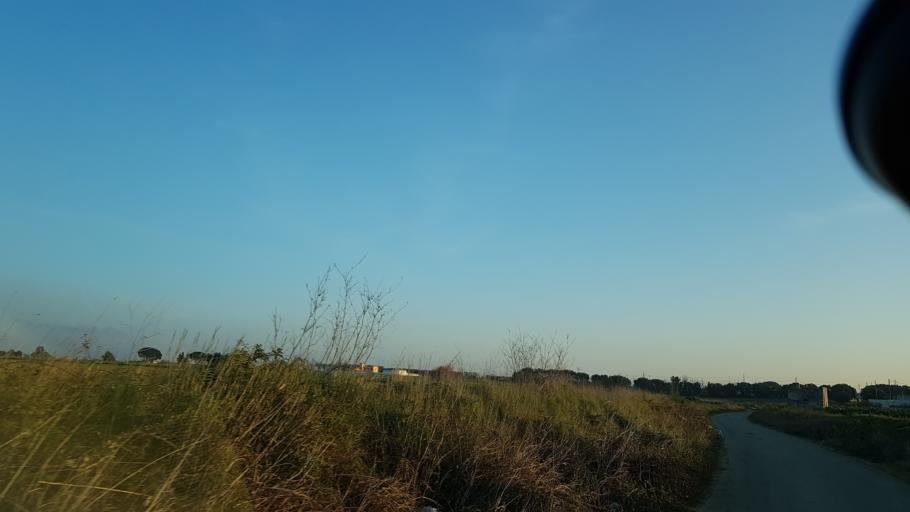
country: IT
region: Apulia
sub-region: Provincia di Brindisi
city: La Rosa
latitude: 40.6157
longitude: 17.9403
